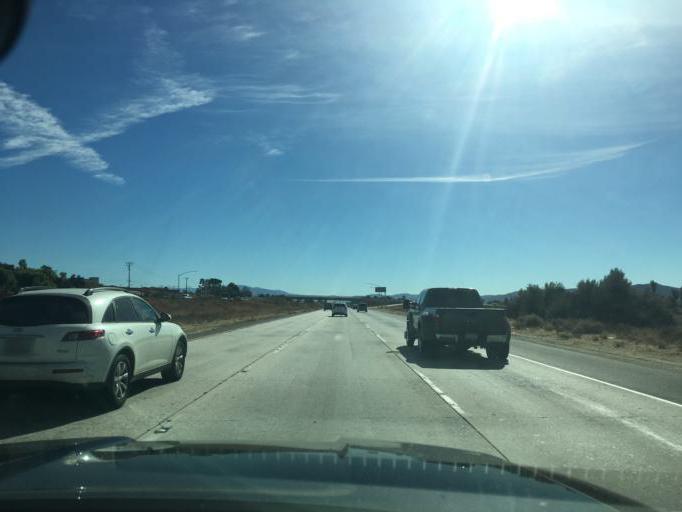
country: US
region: California
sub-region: Riverside County
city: Wildomar
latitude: 33.6175
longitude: -117.2651
